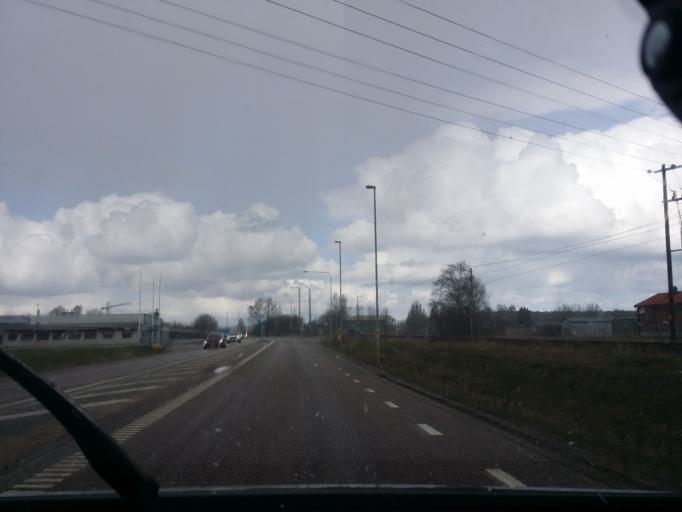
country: SE
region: Vaestmanland
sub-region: Sala Kommun
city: Sala
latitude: 59.9111
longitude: 16.6194
